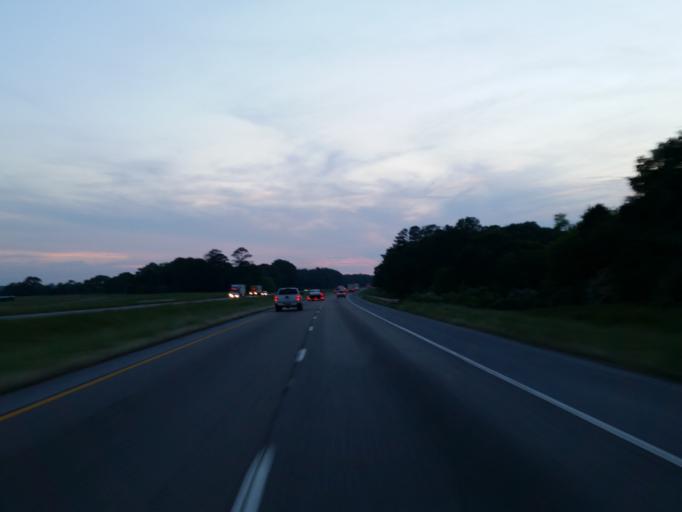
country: US
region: Alabama
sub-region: Talladega County
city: Lincoln
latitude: 33.5850
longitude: -86.0658
